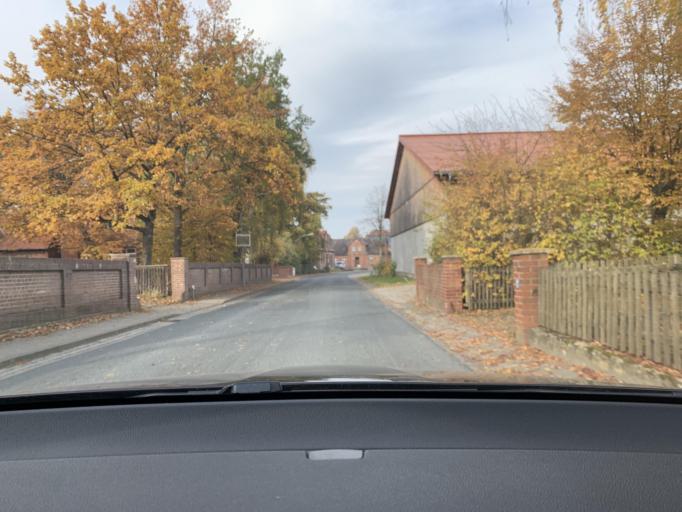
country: DE
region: Lower Saxony
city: Meine
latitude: 52.3800
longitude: 10.5448
